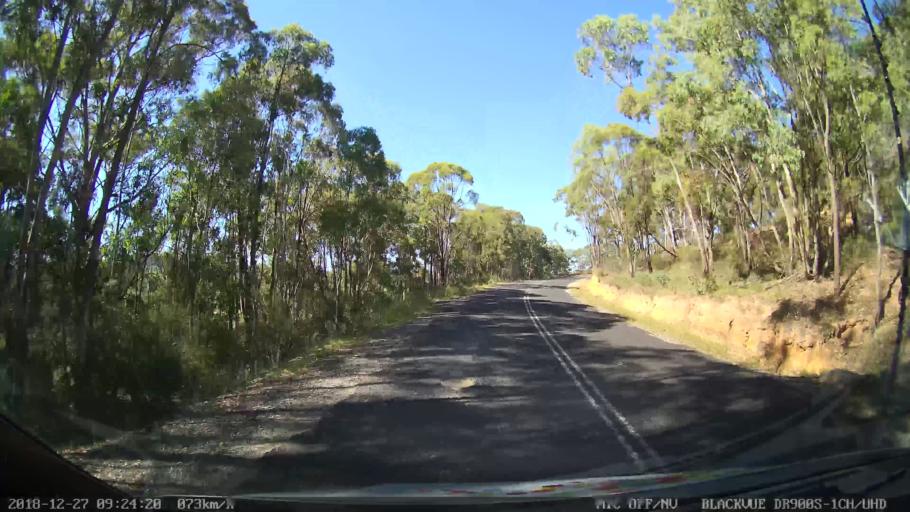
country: AU
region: New South Wales
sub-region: Lithgow
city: Portland
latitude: -33.1357
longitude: 149.9979
